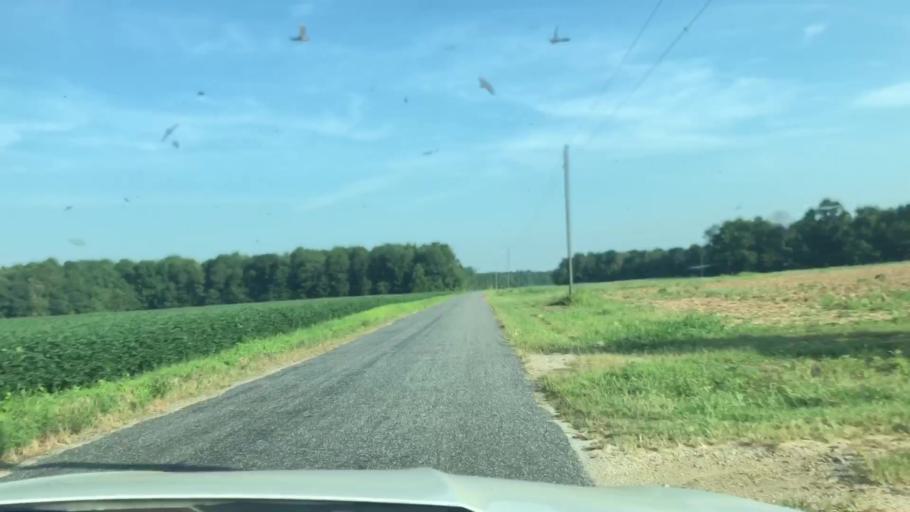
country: US
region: Virginia
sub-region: Middlesex County
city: Saluda
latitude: 37.6473
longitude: -76.6784
